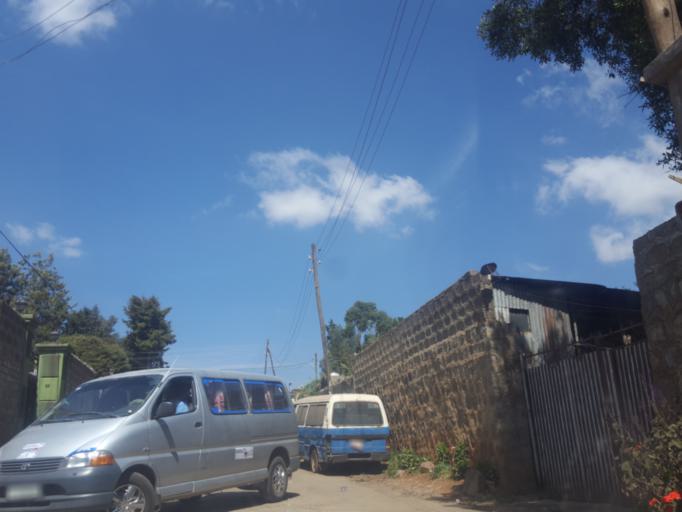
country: ET
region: Adis Abeba
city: Addis Ababa
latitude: 9.0505
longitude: 38.7320
